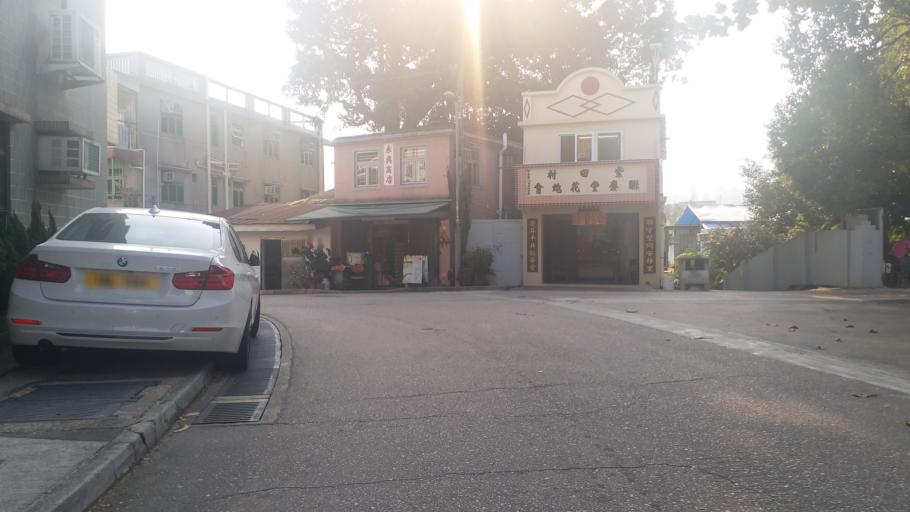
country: HK
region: Tuen Mun
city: Tuen Mun
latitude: 22.4156
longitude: 113.9744
